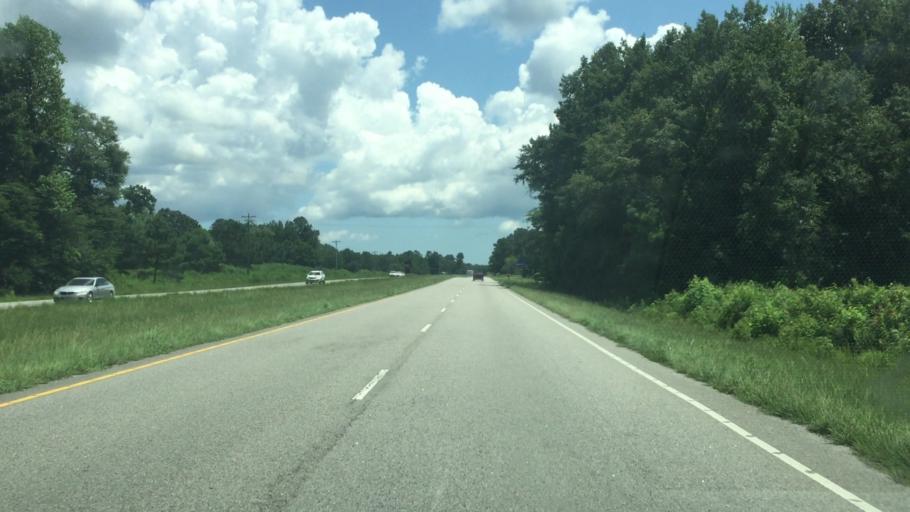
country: US
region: South Carolina
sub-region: Horry County
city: Loris
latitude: 34.0049
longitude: -78.7605
